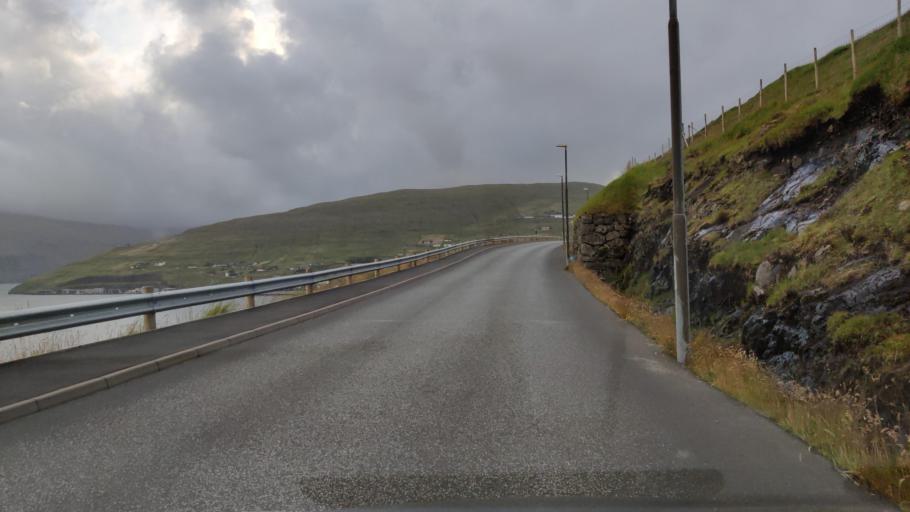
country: FO
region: Streymoy
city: Vestmanna
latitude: 62.1552
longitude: -7.1531
